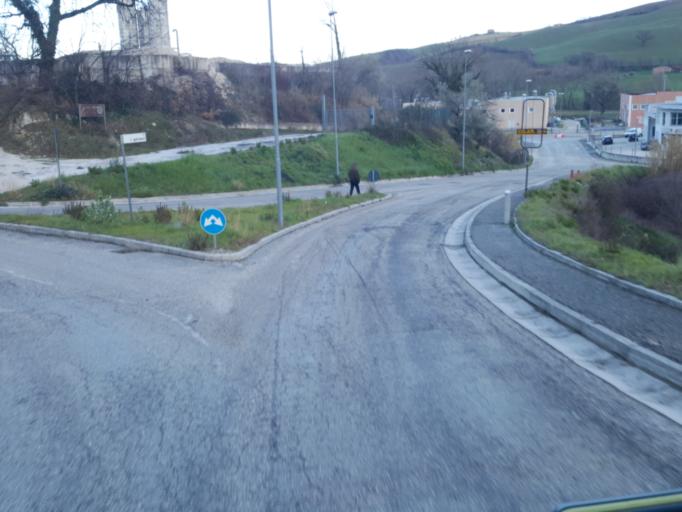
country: IT
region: The Marches
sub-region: Provincia di Macerata
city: San Severino Marche
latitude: 43.2483
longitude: 13.2289
